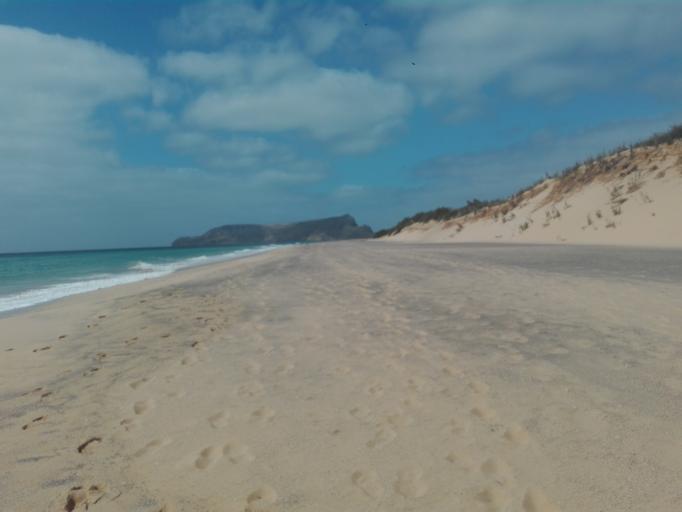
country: PT
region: Madeira
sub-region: Porto Santo
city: Vila de Porto Santo
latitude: 33.0407
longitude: -16.3553
